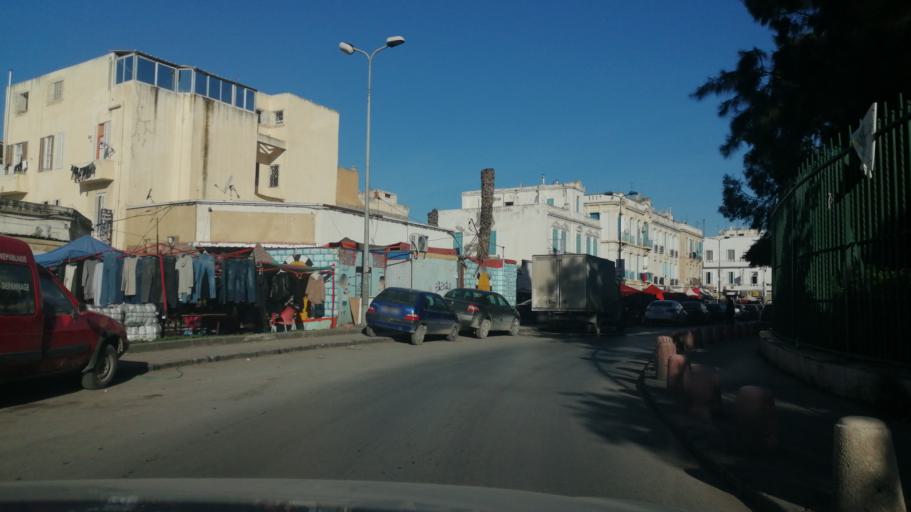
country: TN
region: Tunis
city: Tunis
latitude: 36.8045
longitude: 10.1766
